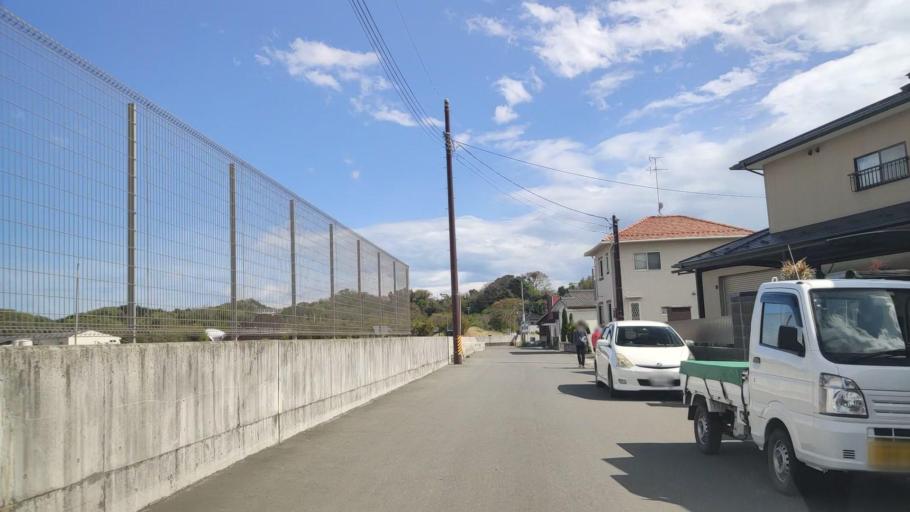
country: JP
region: Miyagi
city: Matsushima
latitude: 38.3394
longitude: 141.1449
